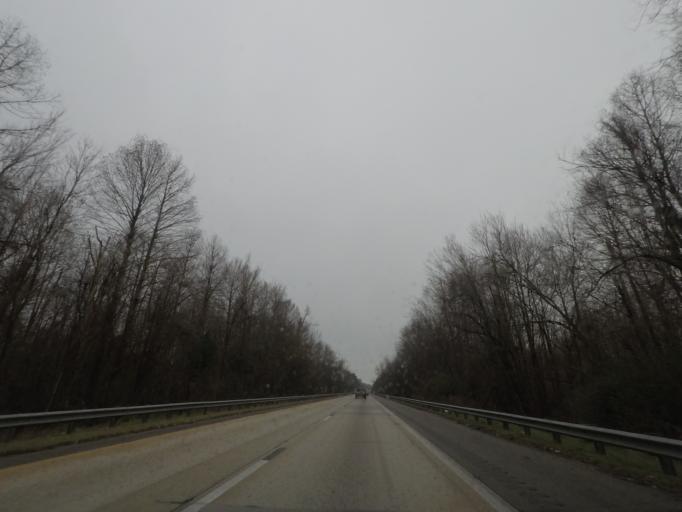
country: US
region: South Carolina
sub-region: Clarendon County
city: Manning
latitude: 33.7285
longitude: -80.2222
